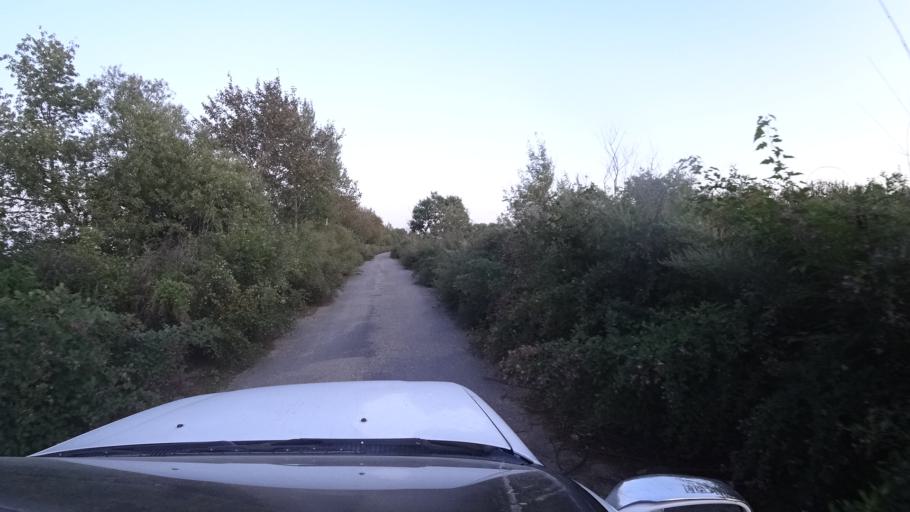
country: RU
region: Primorskiy
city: Dal'nerechensk
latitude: 45.9475
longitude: 133.7631
